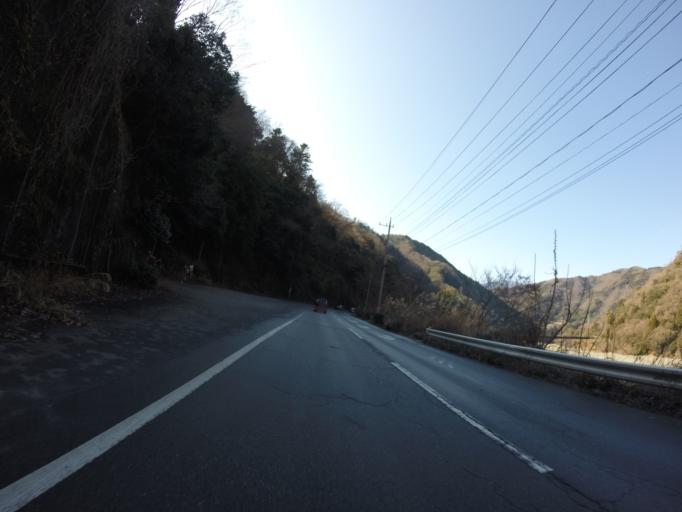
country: JP
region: Yamanashi
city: Ryuo
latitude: 35.4226
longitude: 138.4006
